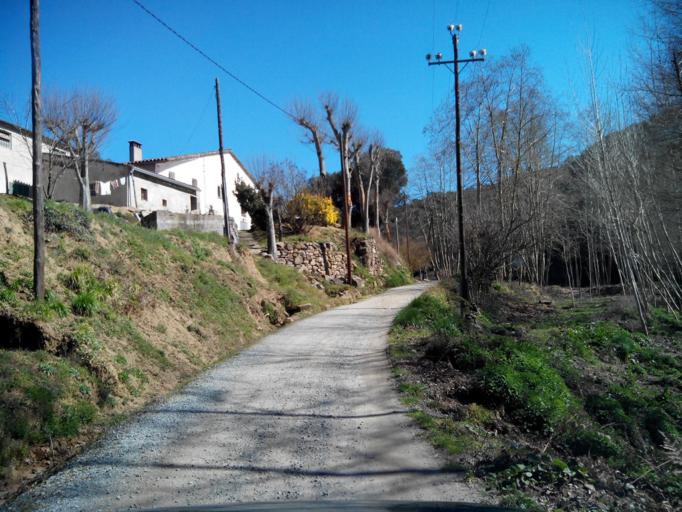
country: ES
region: Catalonia
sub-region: Provincia de Barcelona
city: Sant Andreu de Llavaneres
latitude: 41.6092
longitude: 2.4675
